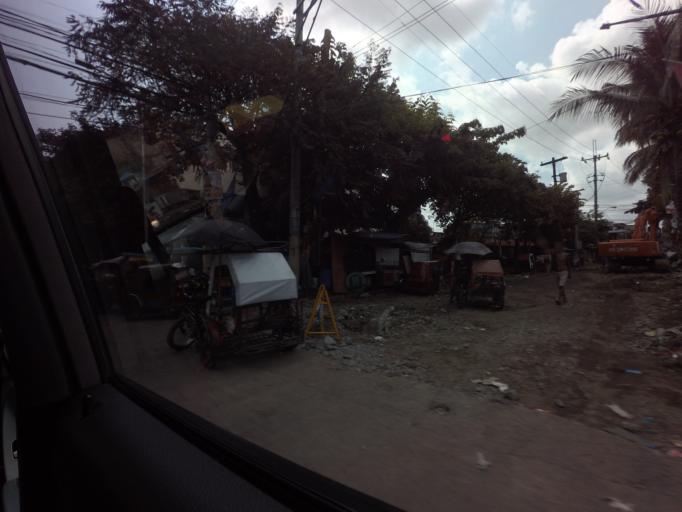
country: PH
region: Metro Manila
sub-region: City of Manila
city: Quiapo
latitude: 14.5990
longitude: 121.0060
